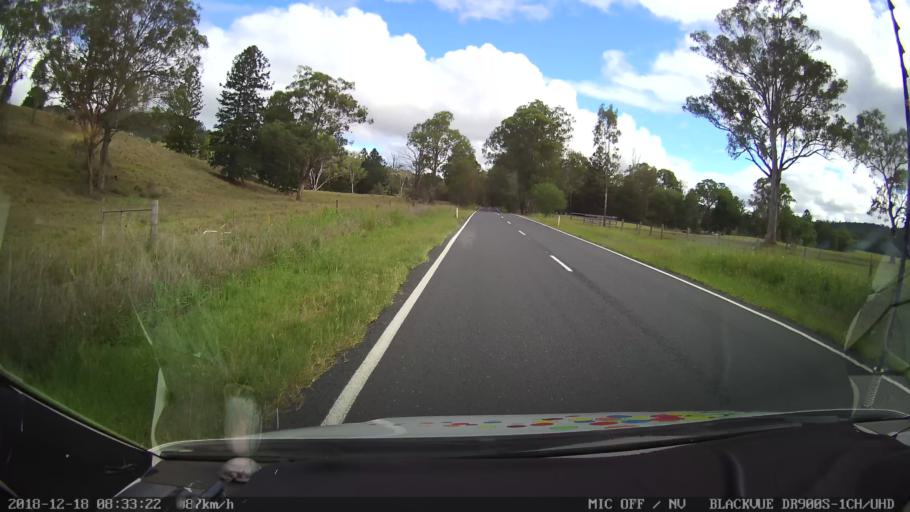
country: AU
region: New South Wales
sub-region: Kyogle
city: Kyogle
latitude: -28.2924
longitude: 152.7860
